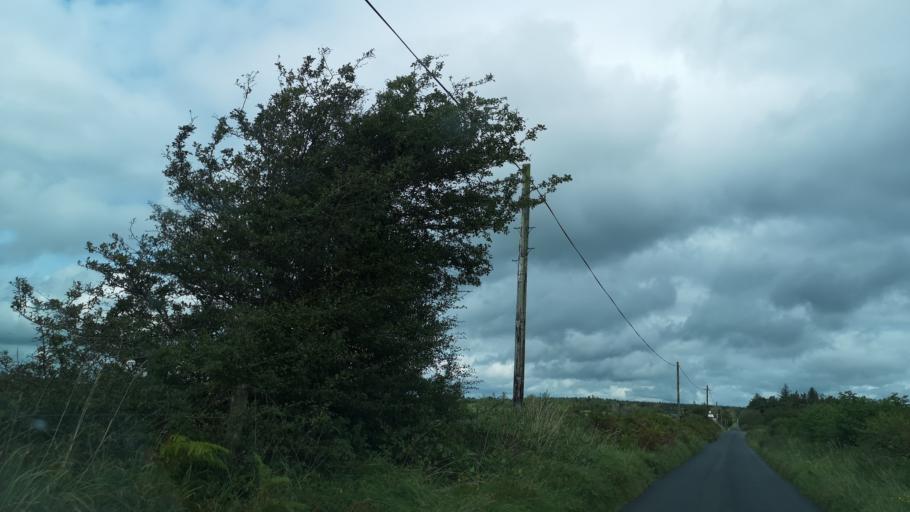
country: IE
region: Connaught
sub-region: County Galway
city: Athenry
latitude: 53.2820
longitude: -8.6684
